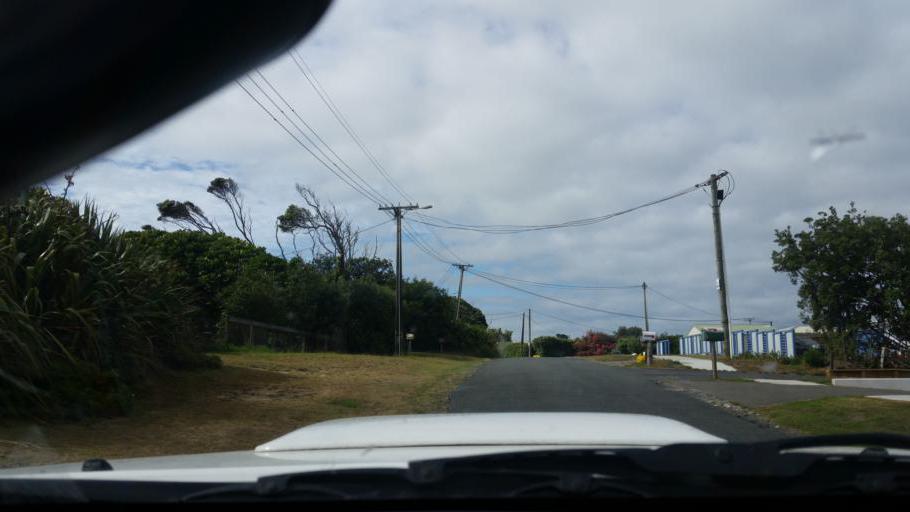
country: NZ
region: Northland
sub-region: Kaipara District
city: Dargaville
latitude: -35.9500
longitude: 173.7463
